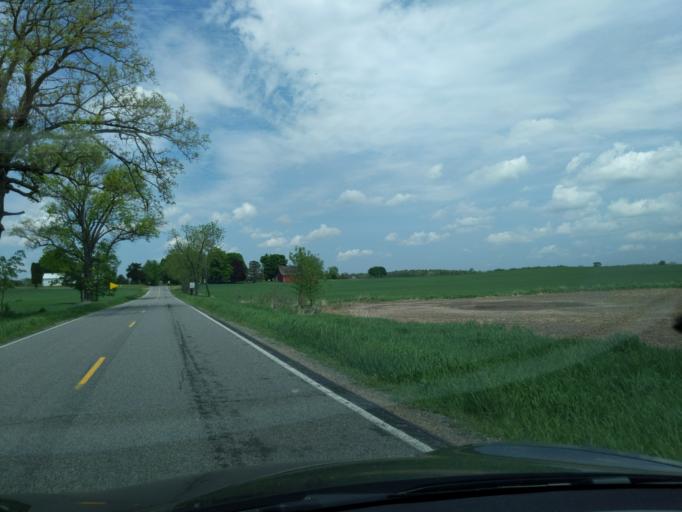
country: US
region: Michigan
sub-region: Ingham County
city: Stockbridge
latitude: 42.4787
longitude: -84.1602
